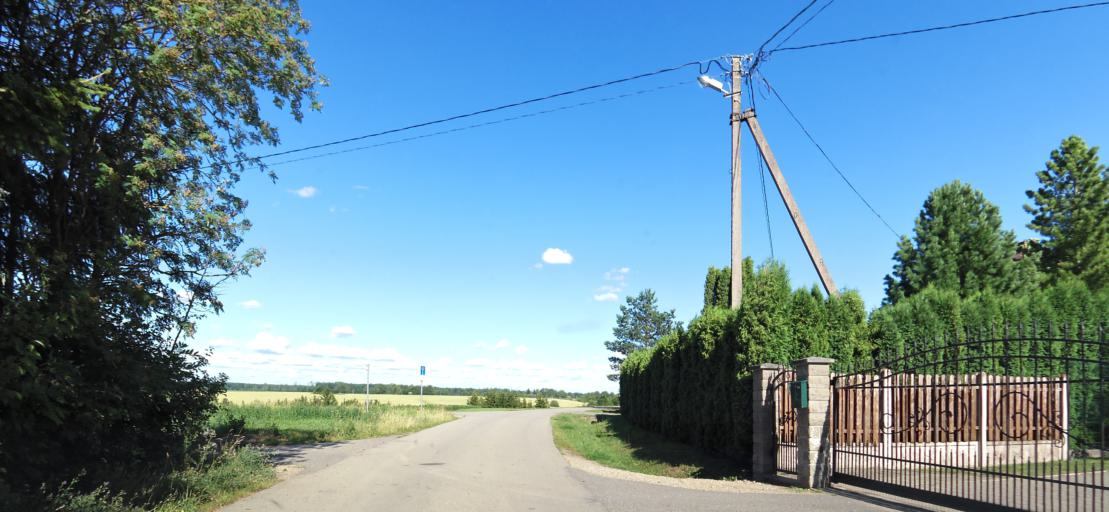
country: LT
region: Panevezys
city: Pasvalys
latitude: 56.1539
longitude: 24.4461
